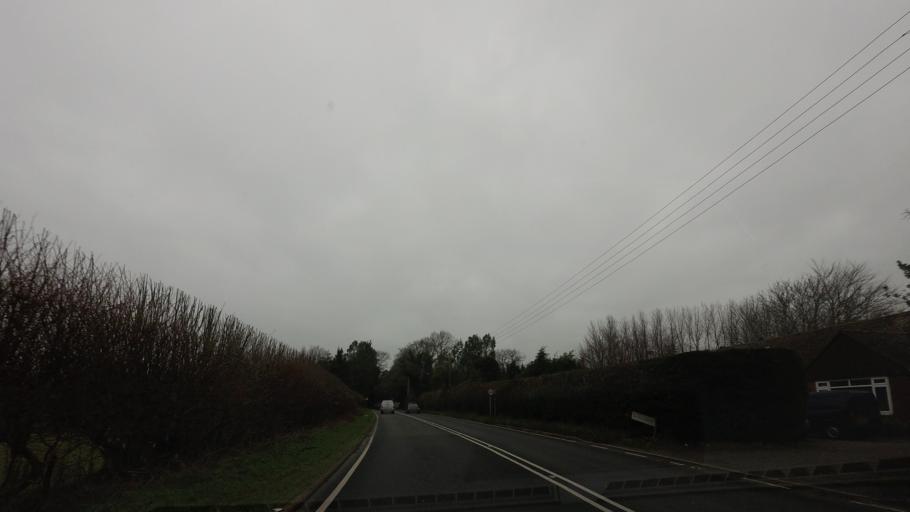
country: GB
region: England
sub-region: East Sussex
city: Battle
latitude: 50.9486
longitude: 0.5074
